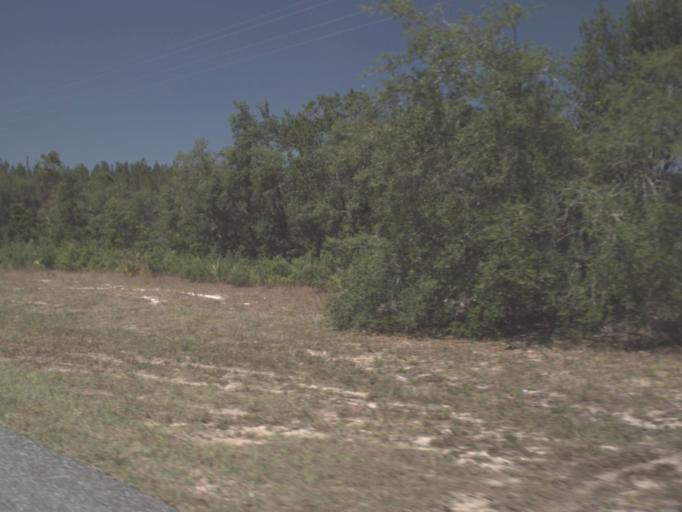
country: US
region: Florida
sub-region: Lake County
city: Astor
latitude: 29.1337
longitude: -81.6247
